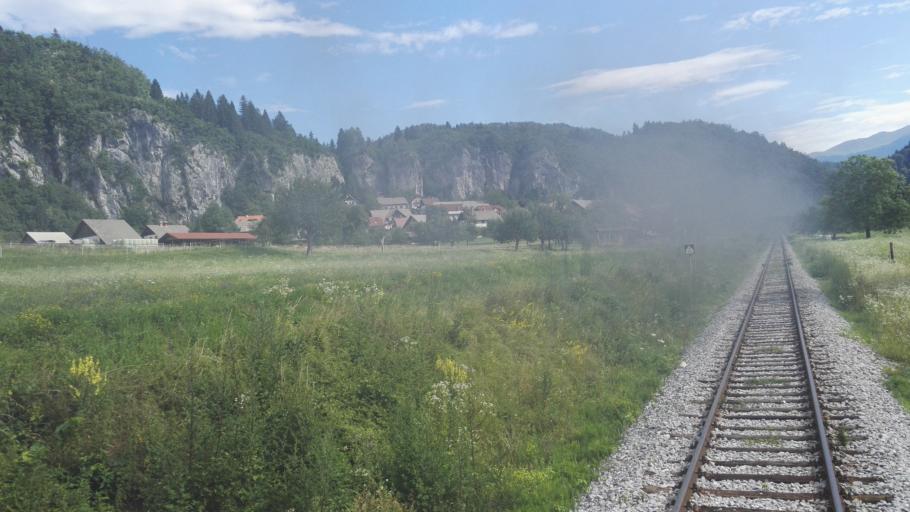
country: SI
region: Gorje
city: Zgornje Gorje
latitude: 46.3437
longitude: 14.0602
